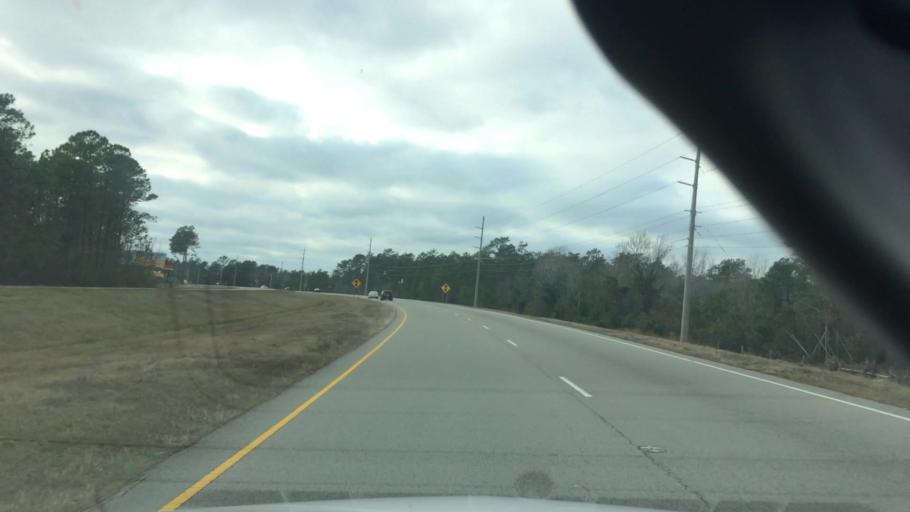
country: US
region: North Carolina
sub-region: Brunswick County
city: Shallotte
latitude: 33.9895
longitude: -78.3848
